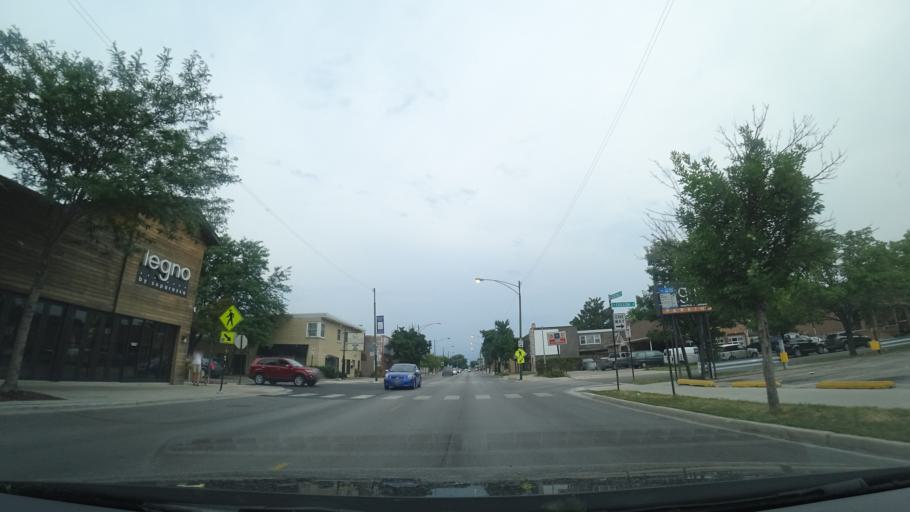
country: US
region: Illinois
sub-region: Cook County
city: Harwood Heights
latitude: 41.9583
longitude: -87.7672
